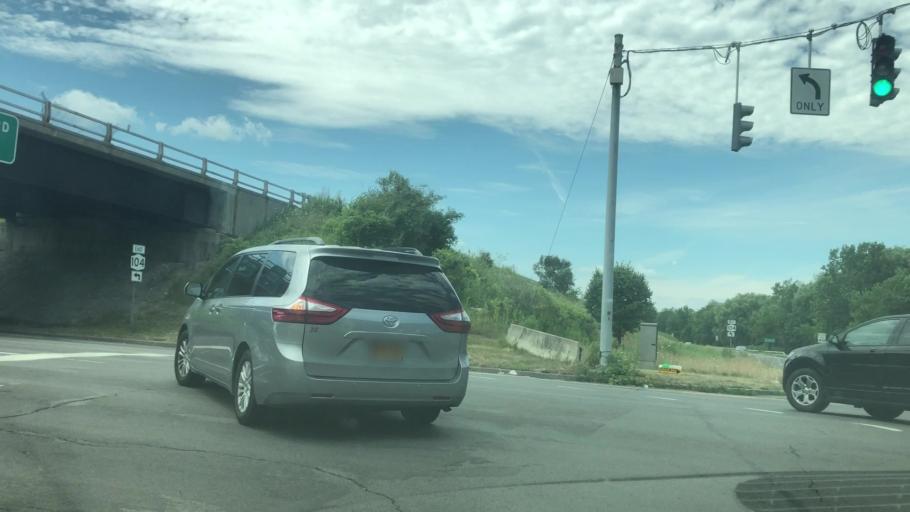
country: US
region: New York
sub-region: Monroe County
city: Webster
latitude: 43.2159
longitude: -77.4465
